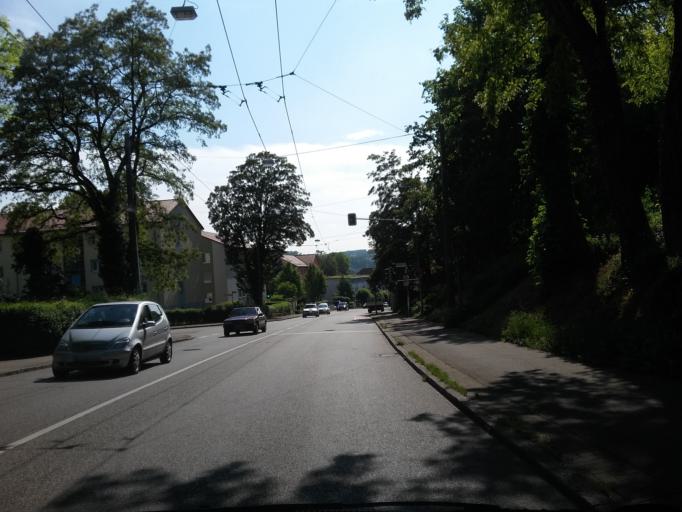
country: DE
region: Baden-Wuerttemberg
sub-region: Regierungsbezirk Stuttgart
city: Esslingen
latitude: 48.7333
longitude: 9.3404
